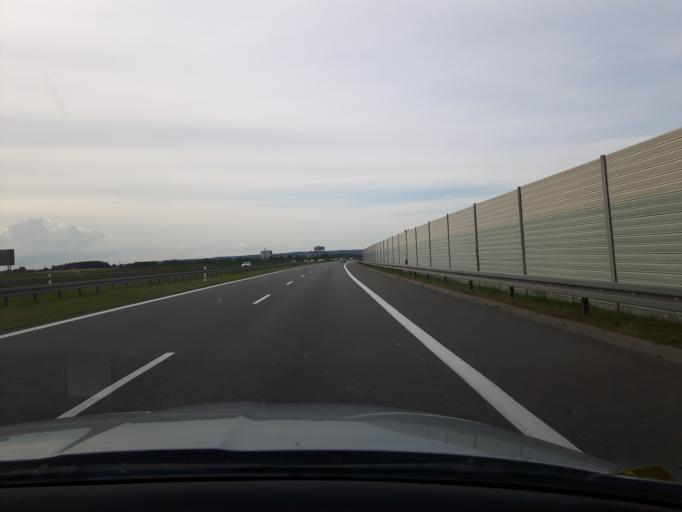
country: PL
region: Warmian-Masurian Voivodeship
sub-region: Powiat elblaski
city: Paslek
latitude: 54.0593
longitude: 19.6296
